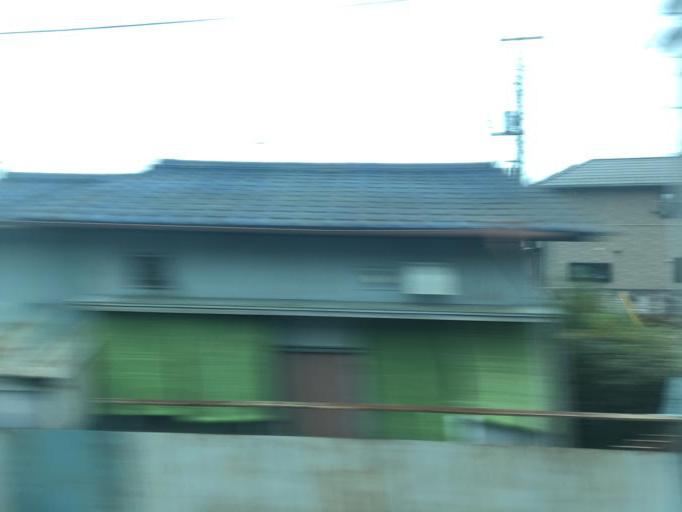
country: JP
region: Ibaraki
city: Shimodate
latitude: 36.3072
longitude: 139.9957
